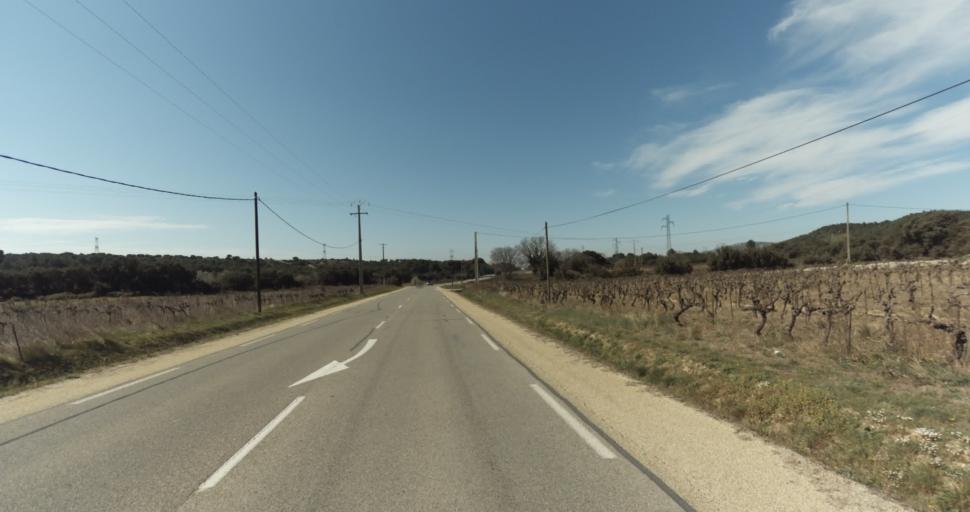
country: FR
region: Provence-Alpes-Cote d'Azur
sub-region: Departement des Bouches-du-Rhone
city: Vernegues
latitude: 43.6463
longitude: 5.2059
